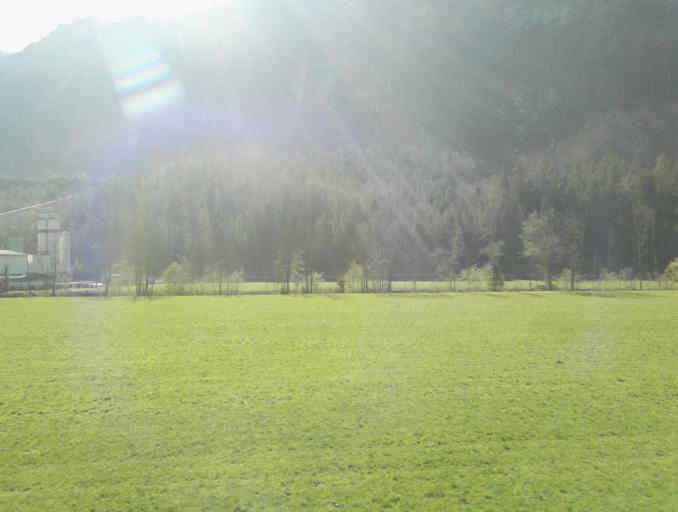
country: AT
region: Salzburg
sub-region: Politischer Bezirk Sankt Johann im Pongau
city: Forstau
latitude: 47.3924
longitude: 13.5116
